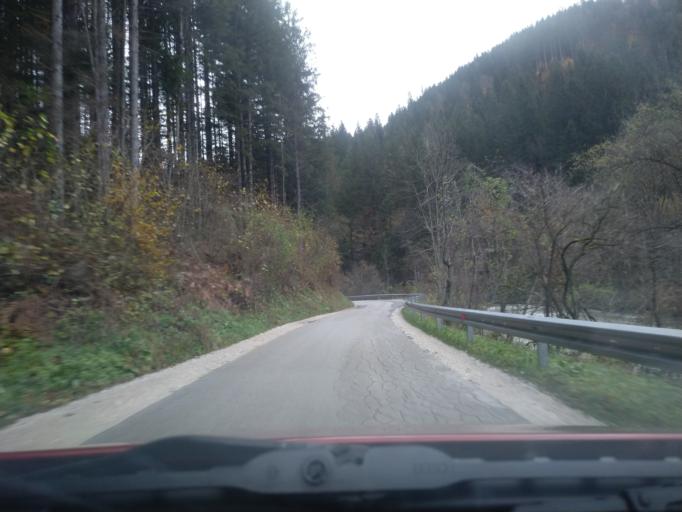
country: SI
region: Luce
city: Luce
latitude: 46.3406
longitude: 14.7304
